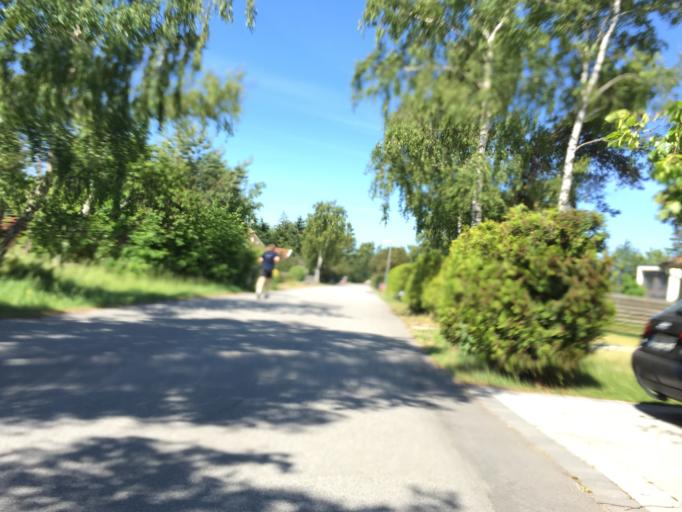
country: SE
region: Skane
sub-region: Trelleborgs Kommun
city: Anderslov
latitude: 55.3491
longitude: 13.2658
